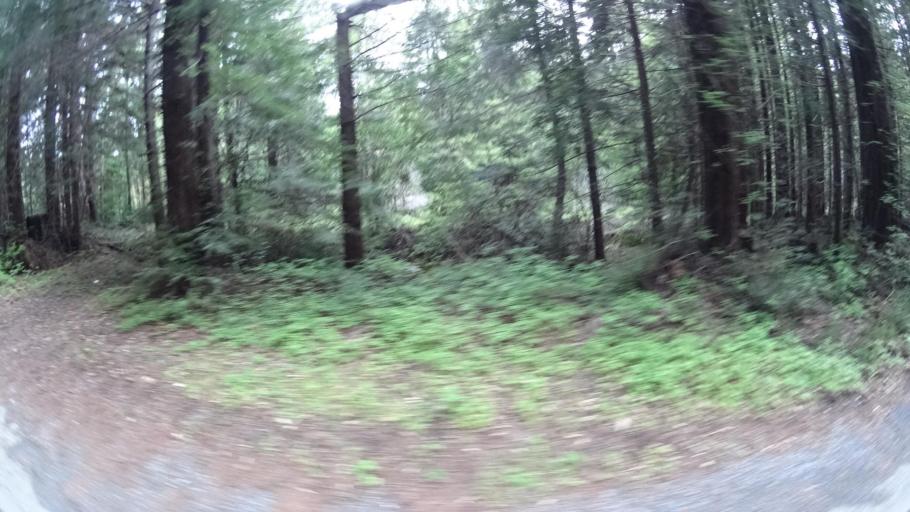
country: US
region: California
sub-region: Humboldt County
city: Redway
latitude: 40.3365
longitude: -123.8563
